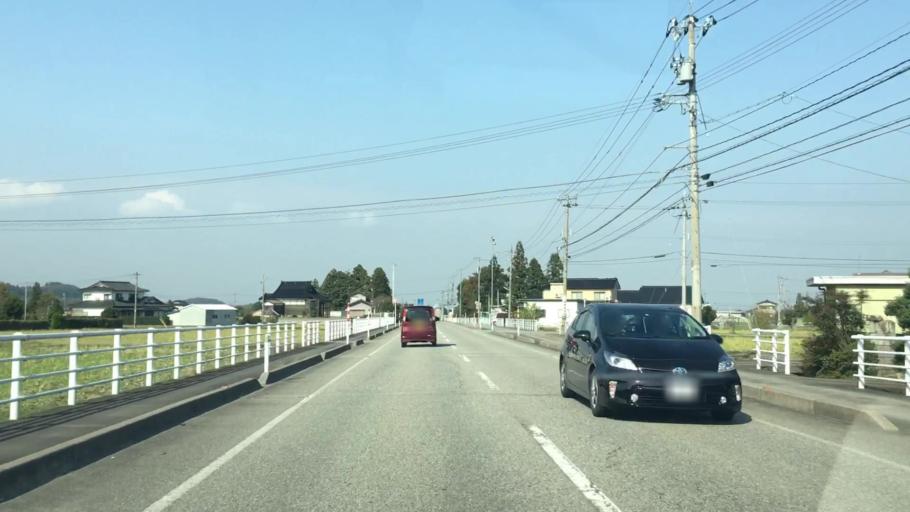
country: JP
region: Toyama
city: Yatsuomachi-higashikumisaka
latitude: 36.5724
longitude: 137.1957
